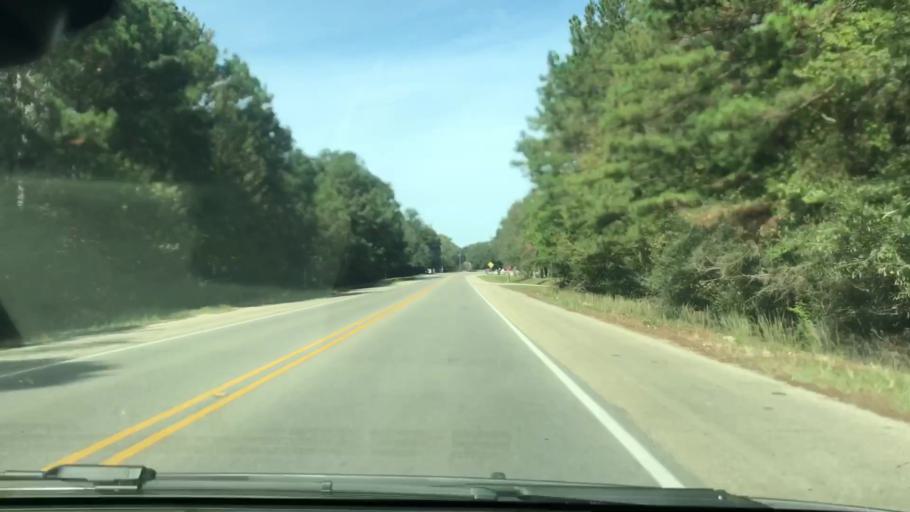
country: US
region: Louisiana
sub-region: Saint Tammany Parish
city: Pearl River
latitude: 30.4228
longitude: -89.7874
